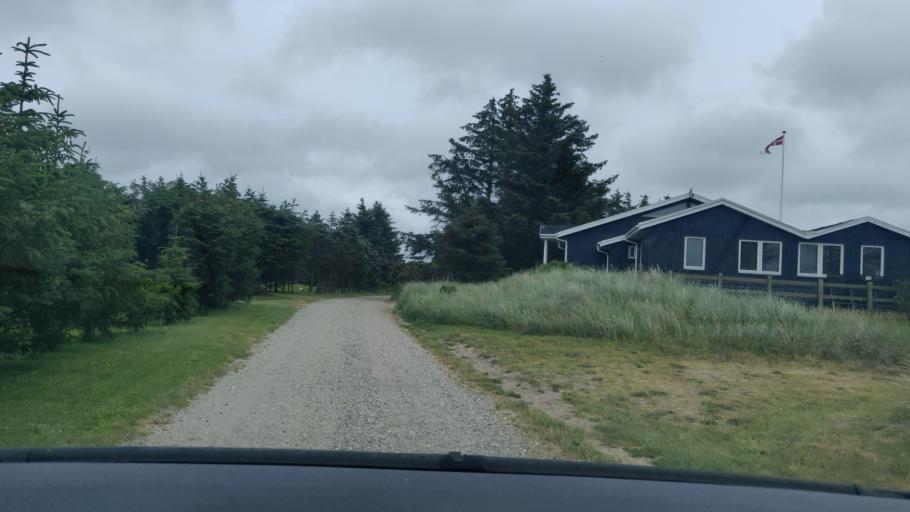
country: DK
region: North Denmark
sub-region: Jammerbugt Kommune
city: Pandrup
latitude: 57.2575
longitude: 9.6003
